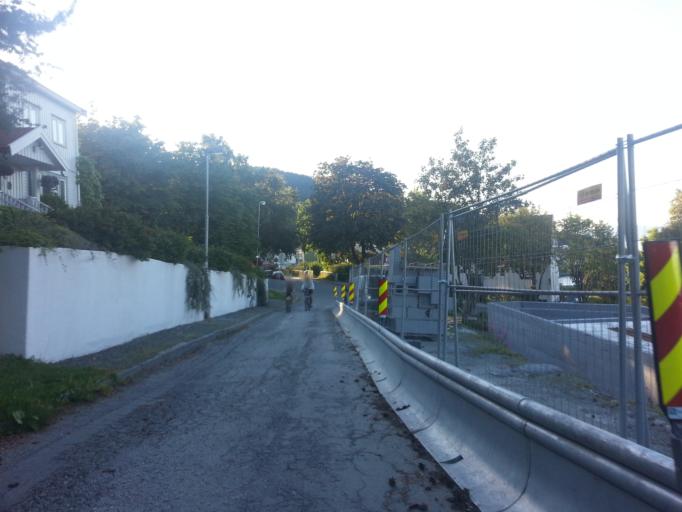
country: NO
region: Sor-Trondelag
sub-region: Trondheim
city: Trondheim
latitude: 63.4273
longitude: 10.3618
